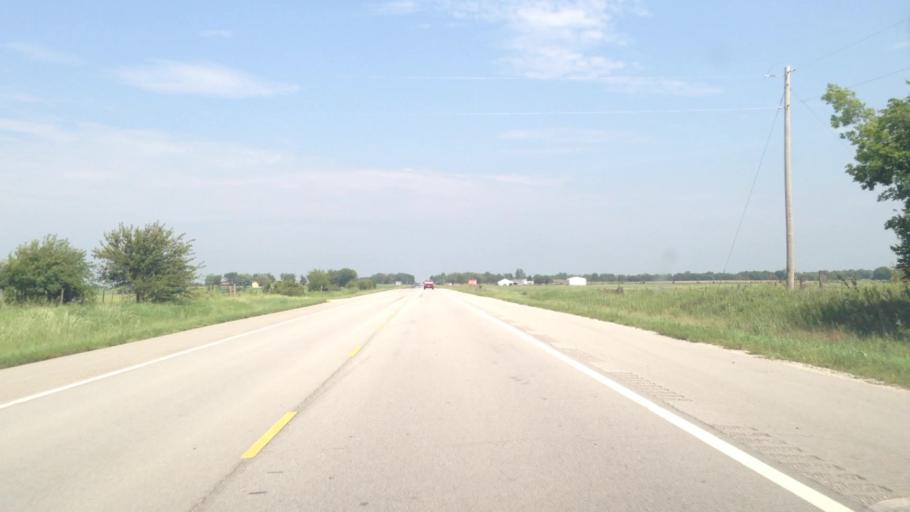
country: US
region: Kansas
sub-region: Labette County
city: Altamont
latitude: 37.2444
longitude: -95.2670
